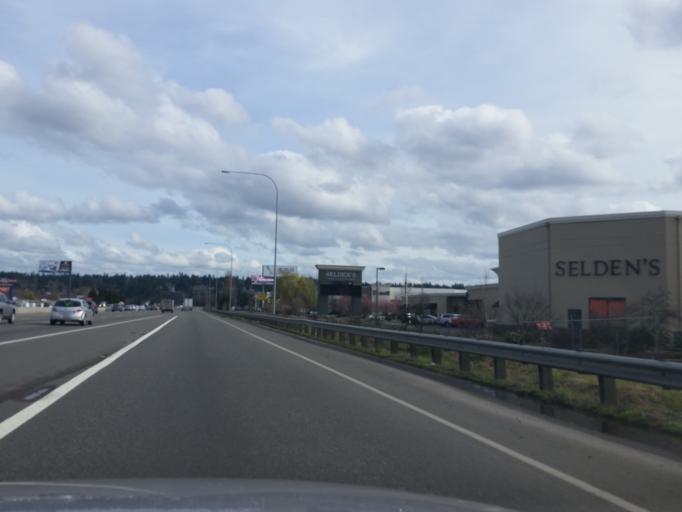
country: US
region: Washington
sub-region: Pierce County
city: Fife
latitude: 47.2408
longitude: -122.3500
